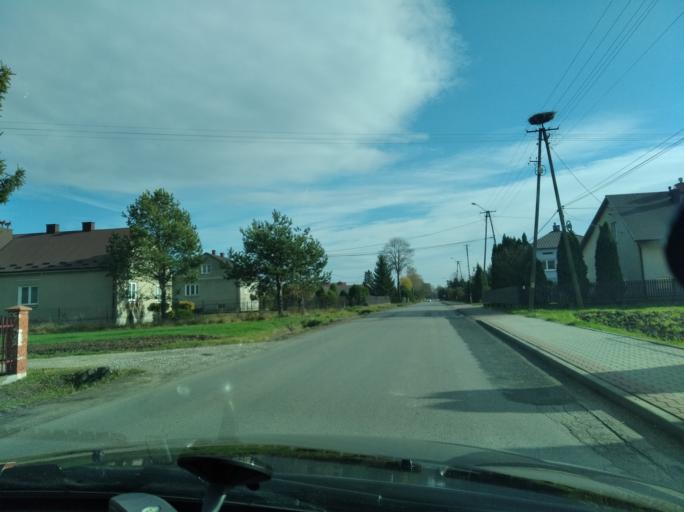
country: PL
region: Subcarpathian Voivodeship
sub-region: Powiat ropczycko-sedziszowski
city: Ostrow
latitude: 50.1008
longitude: 21.6058
